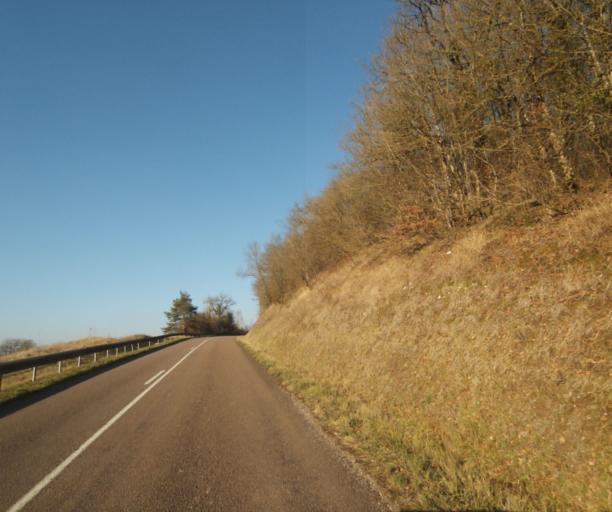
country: FR
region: Champagne-Ardenne
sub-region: Departement de la Haute-Marne
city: Chevillon
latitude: 48.5145
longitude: 5.1190
